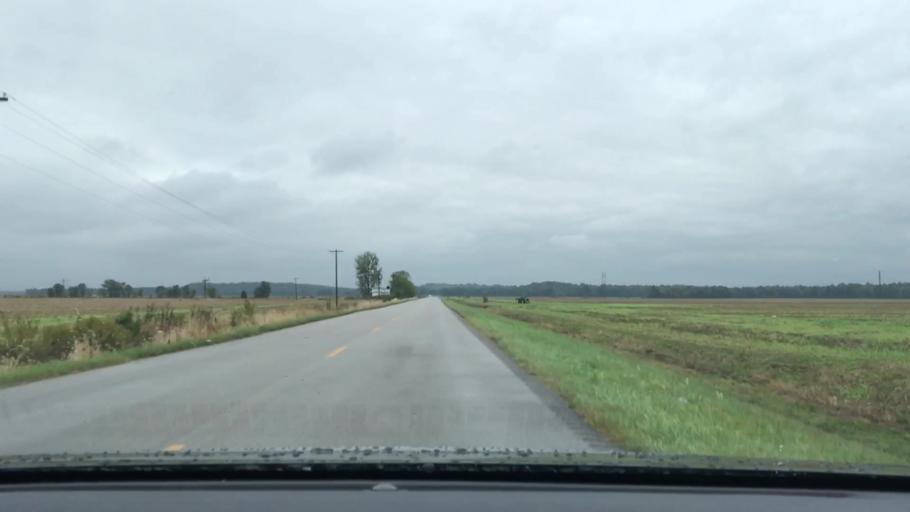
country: US
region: Kentucky
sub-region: McLean County
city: Calhoun
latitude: 37.5118
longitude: -87.2527
